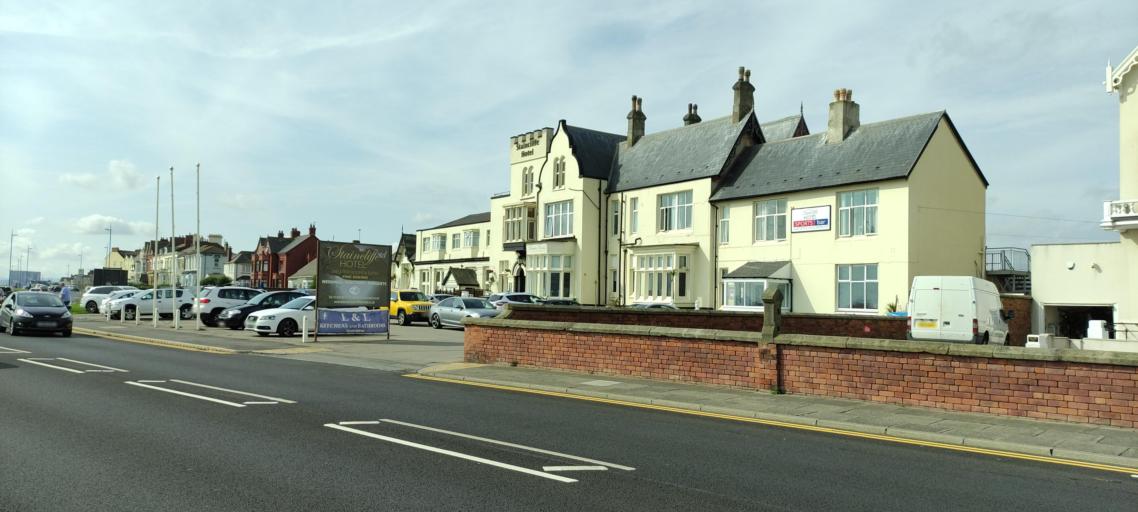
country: GB
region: England
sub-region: Hartlepool
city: Hartlepool
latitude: 54.6664
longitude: -1.1886
